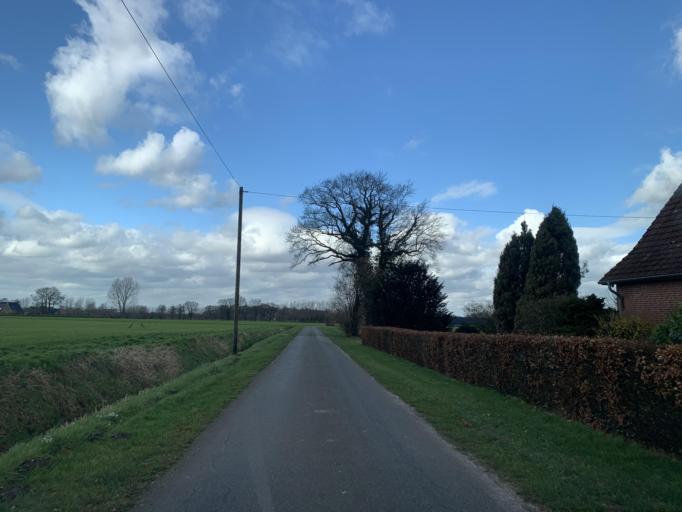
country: DE
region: North Rhine-Westphalia
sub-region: Regierungsbezirk Munster
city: Horstmar
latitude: 52.1097
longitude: 7.3125
